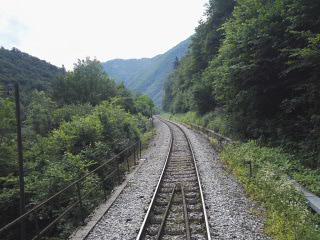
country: SI
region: Tolmin
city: Tolmin
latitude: 46.1557
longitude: 13.8424
